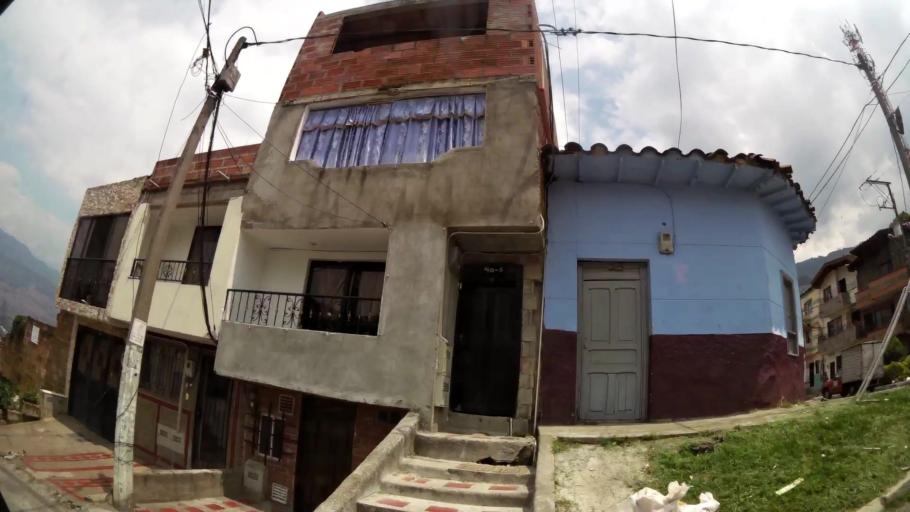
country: CO
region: Antioquia
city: Medellin
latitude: 6.2640
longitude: -75.5510
